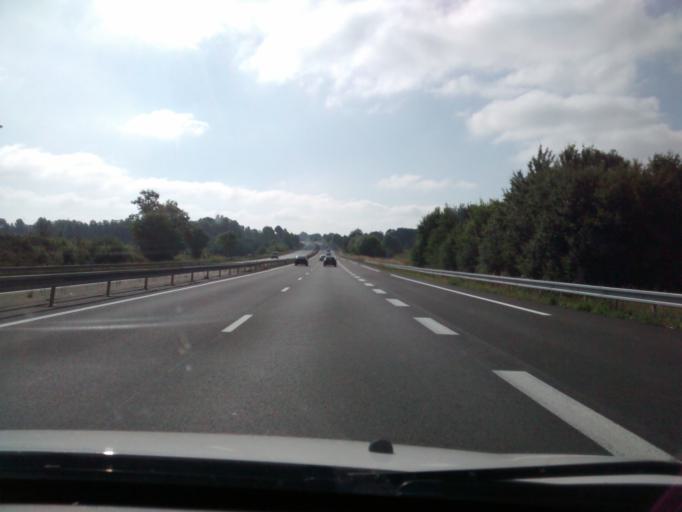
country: FR
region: Pays de la Loire
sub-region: Departement de la Mayenne
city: Vaiges
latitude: 48.0551
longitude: -0.4783
